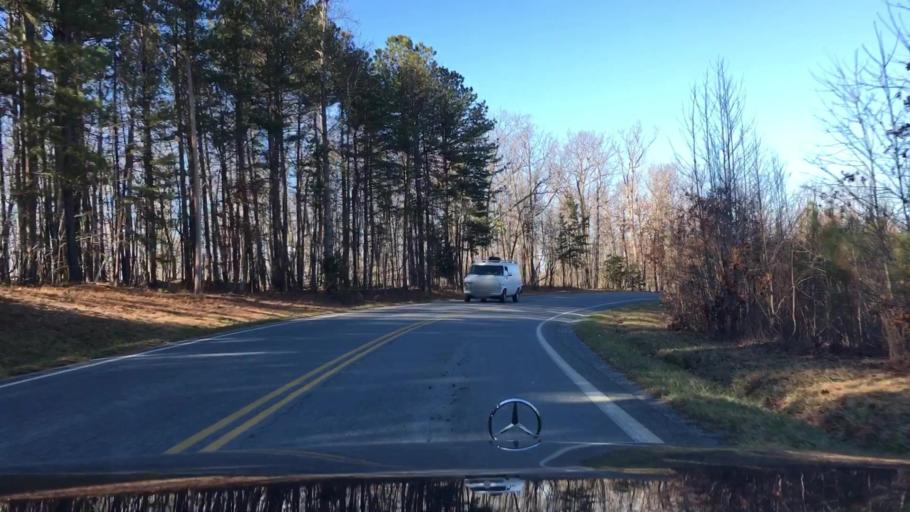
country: US
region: Virginia
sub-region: Pittsylvania County
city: Motley
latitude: 37.1664
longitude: -79.4051
